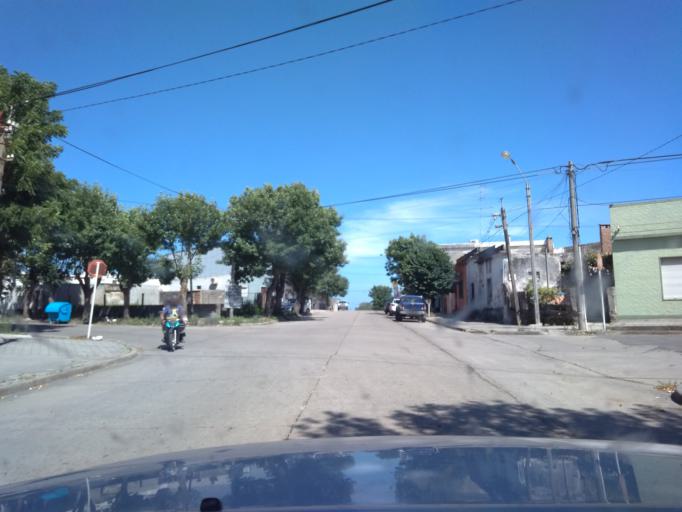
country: UY
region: Florida
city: Florida
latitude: -34.0909
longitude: -56.2173
